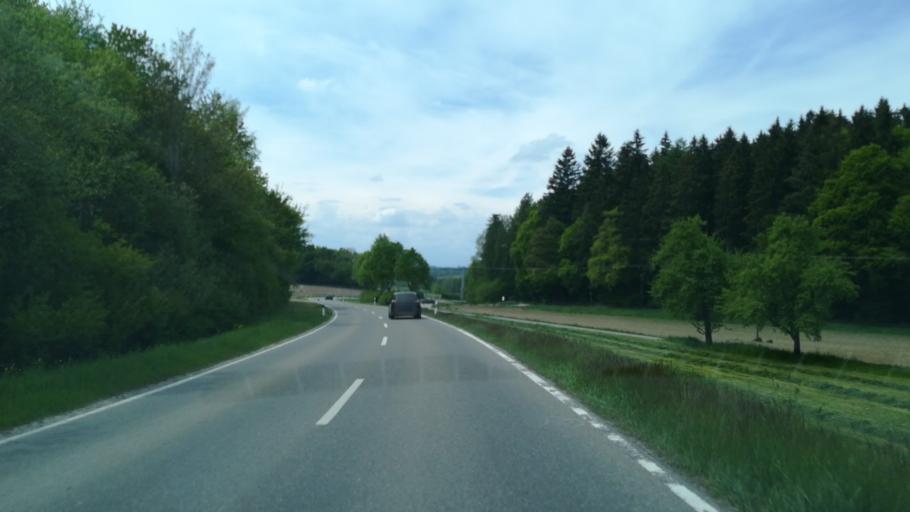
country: DE
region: Baden-Wuerttemberg
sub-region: Freiburg Region
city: Muhlingen
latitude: 47.8874
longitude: 9.0396
